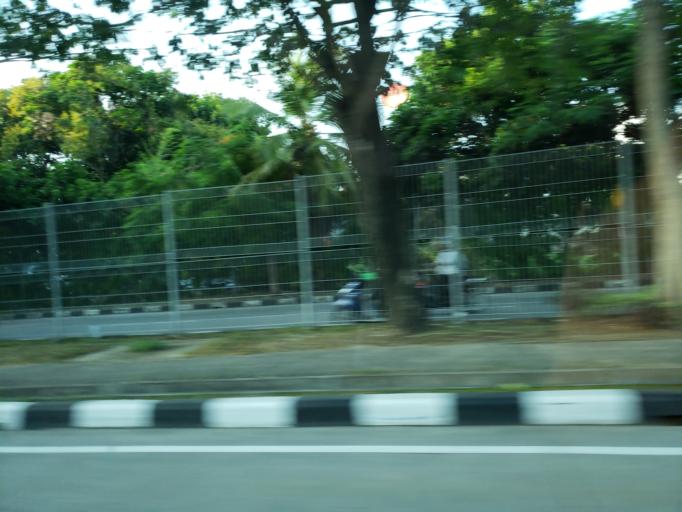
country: ID
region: Bali
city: Kelanabian
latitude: -8.7408
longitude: 115.1669
